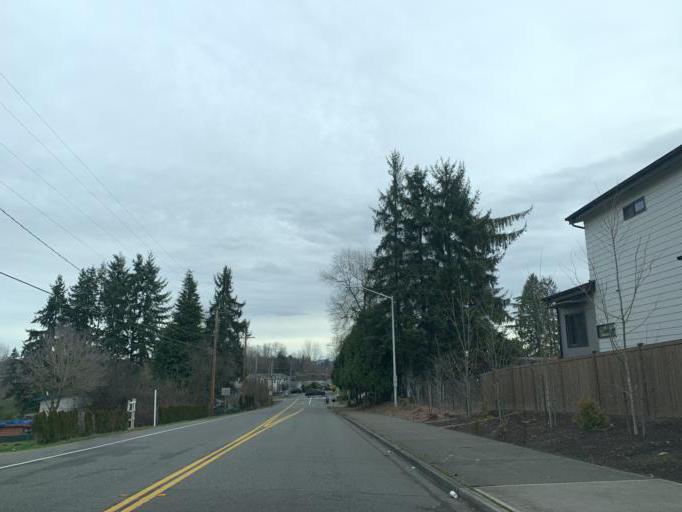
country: US
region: Washington
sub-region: King County
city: Lea Hill
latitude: 47.3598
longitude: -122.1783
